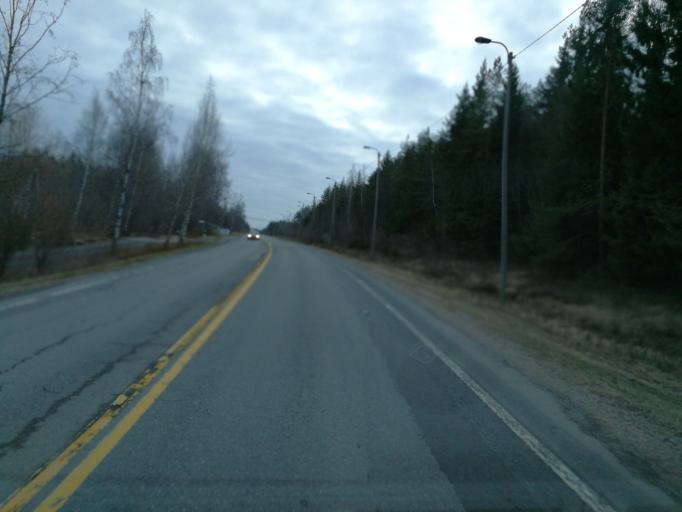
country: FI
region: Varsinais-Suomi
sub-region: Turku
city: Paimio
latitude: 60.4183
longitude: 22.6820
